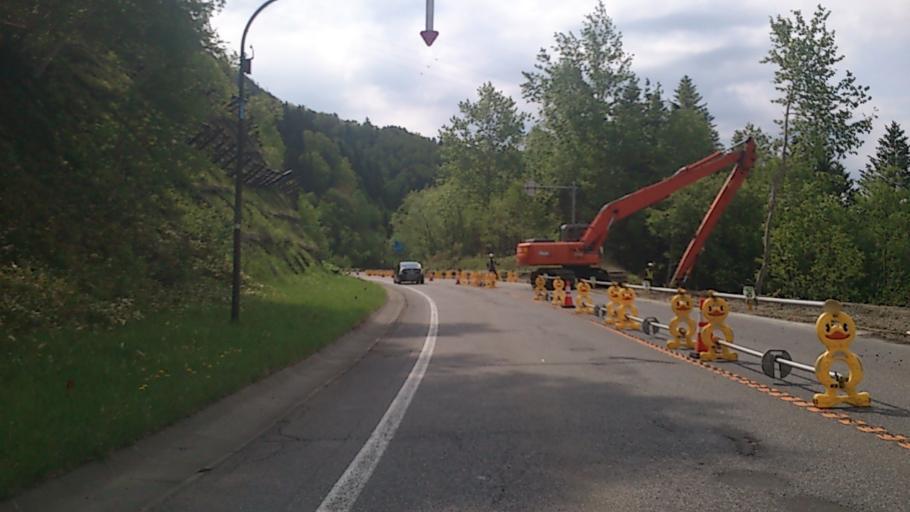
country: JP
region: Hokkaido
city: Kamikawa
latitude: 43.6837
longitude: 143.0333
